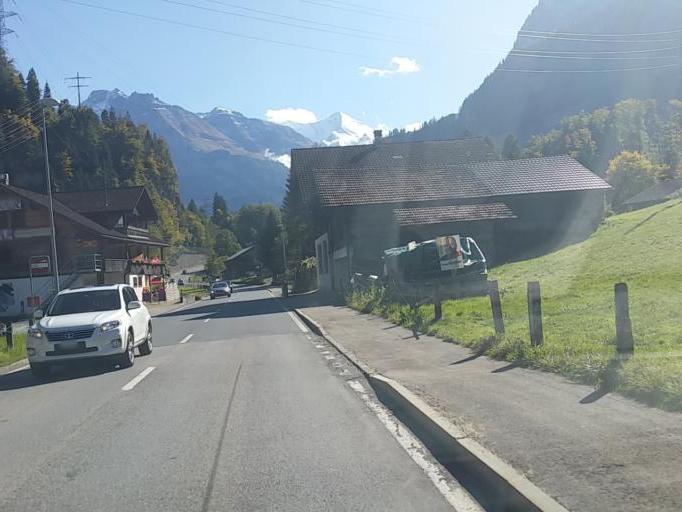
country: CH
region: Bern
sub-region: Frutigen-Niedersimmental District
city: Kandersteg
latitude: 46.5402
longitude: 7.6671
